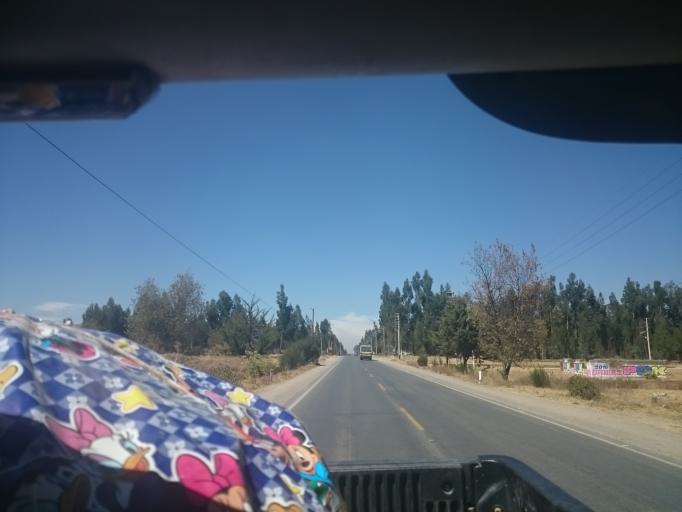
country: PE
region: Junin
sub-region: Provincia de Concepcion
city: Matahuasi
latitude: -11.8998
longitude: -75.3369
